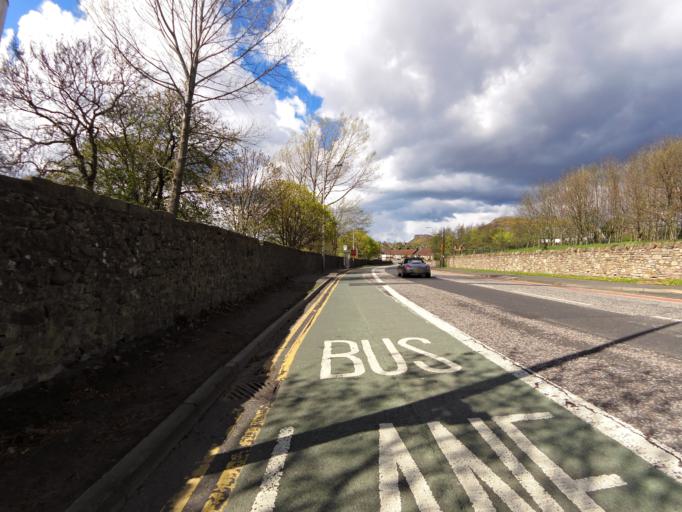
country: GB
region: Scotland
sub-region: West Lothian
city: Seafield
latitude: 55.9258
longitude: -3.1535
